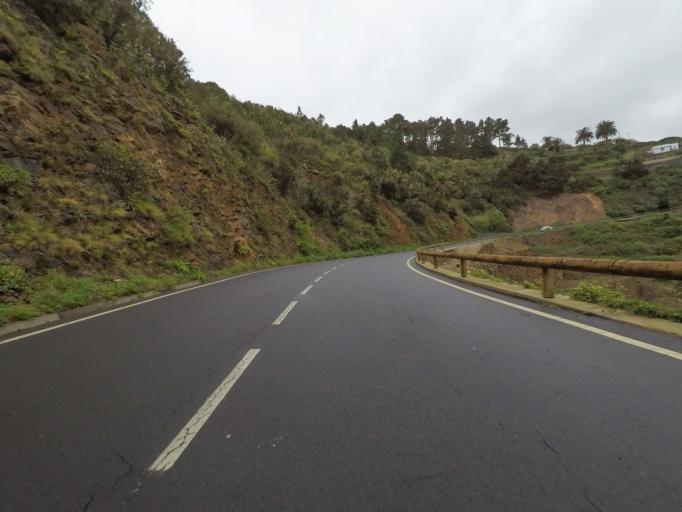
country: ES
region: Canary Islands
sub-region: Provincia de Santa Cruz de Tenerife
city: Agulo
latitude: 28.1872
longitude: -17.2177
